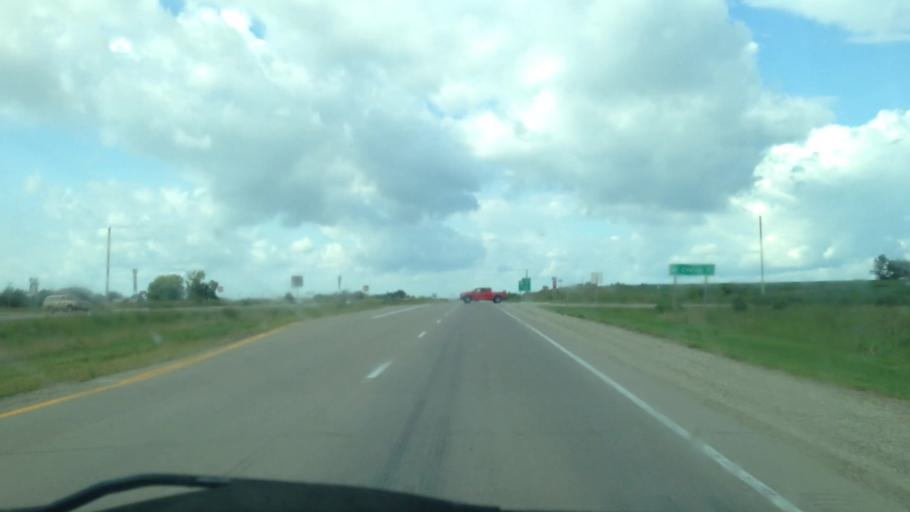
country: US
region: Illinois
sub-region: Hancock County
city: Nauvoo
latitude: 40.5893
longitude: -91.5635
